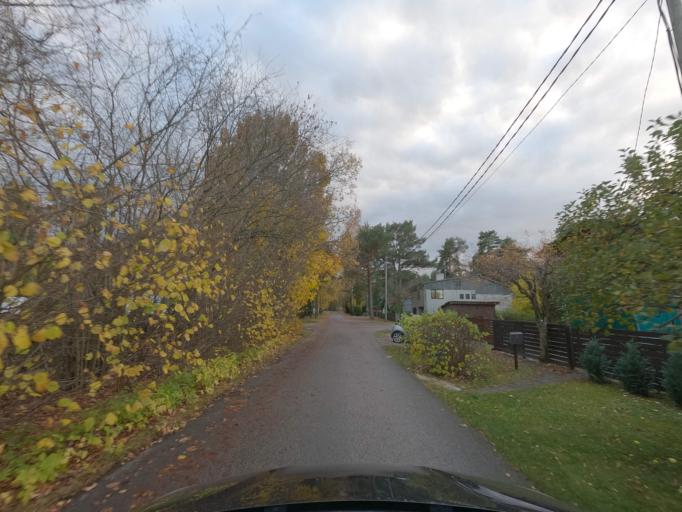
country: EE
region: Harju
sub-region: Saue linn
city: Saue
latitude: 59.3145
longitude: 24.5423
